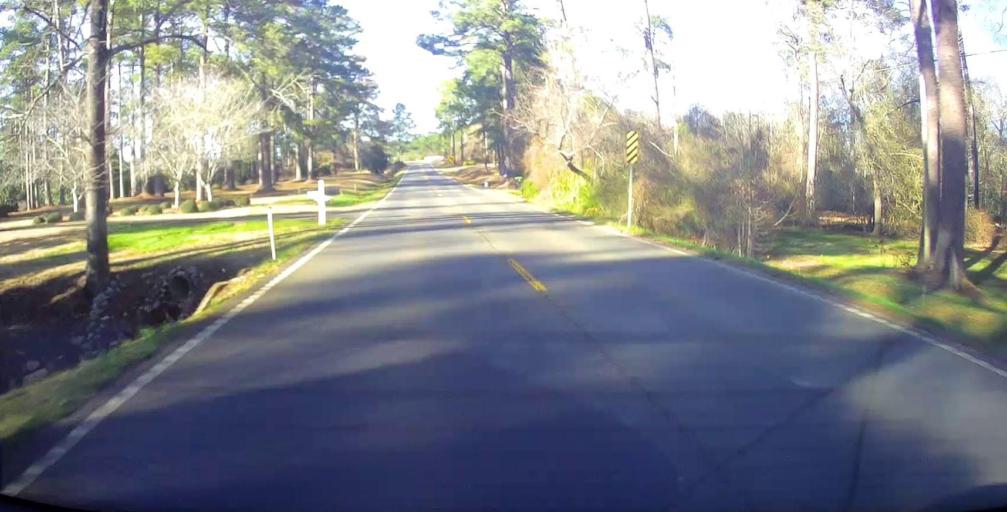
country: US
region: Georgia
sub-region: Sumter County
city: Americus
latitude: 32.0288
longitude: -84.2190
